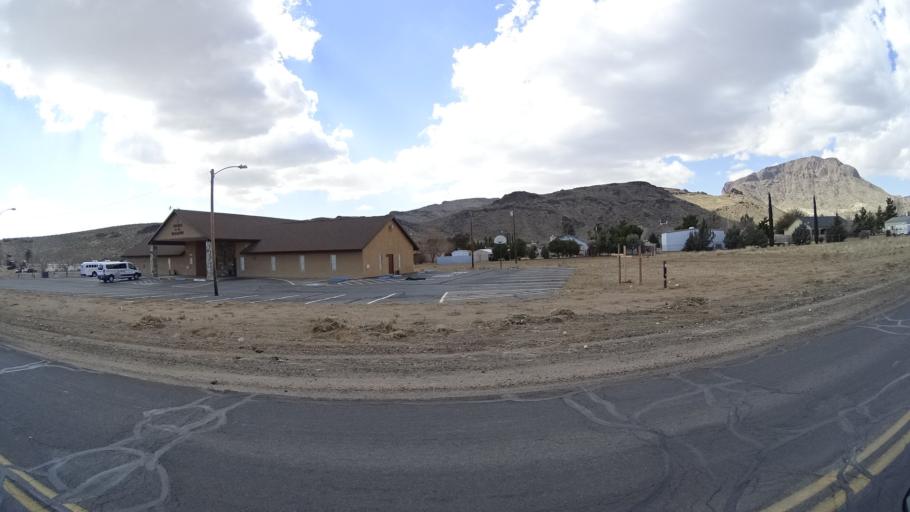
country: US
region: Arizona
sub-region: Mohave County
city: New Kingman-Butler
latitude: 35.2608
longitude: -114.0392
